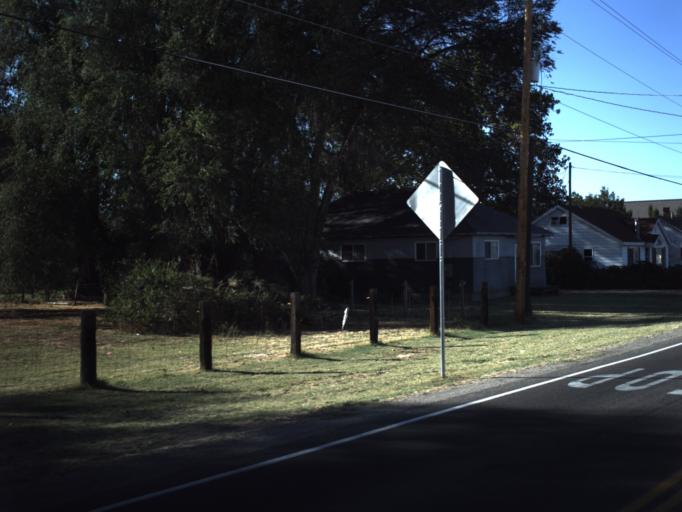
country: US
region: Utah
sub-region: Weber County
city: Hooper
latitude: 41.1650
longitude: -112.1227
